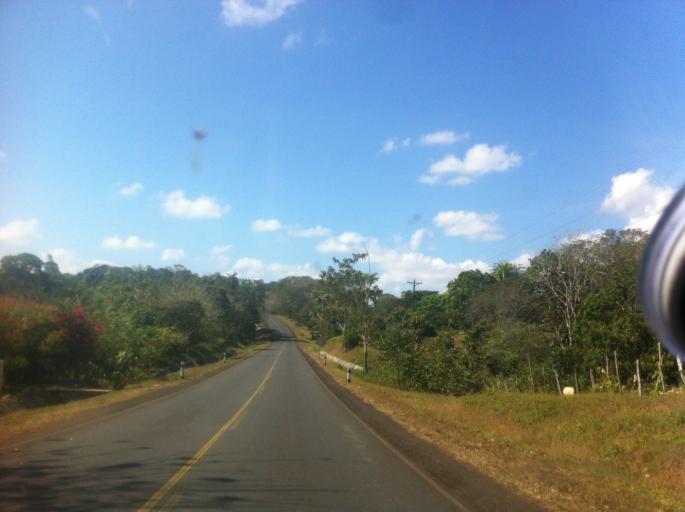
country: NI
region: Rio San Juan
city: San Carlos
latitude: 11.1674
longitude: -84.7450
